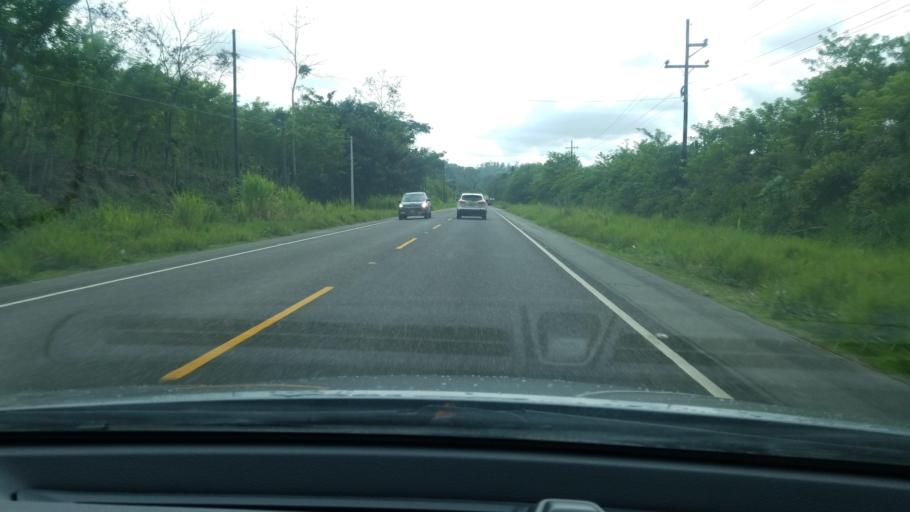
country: HN
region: Cortes
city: Potrerillos
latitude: 15.6147
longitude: -88.2780
